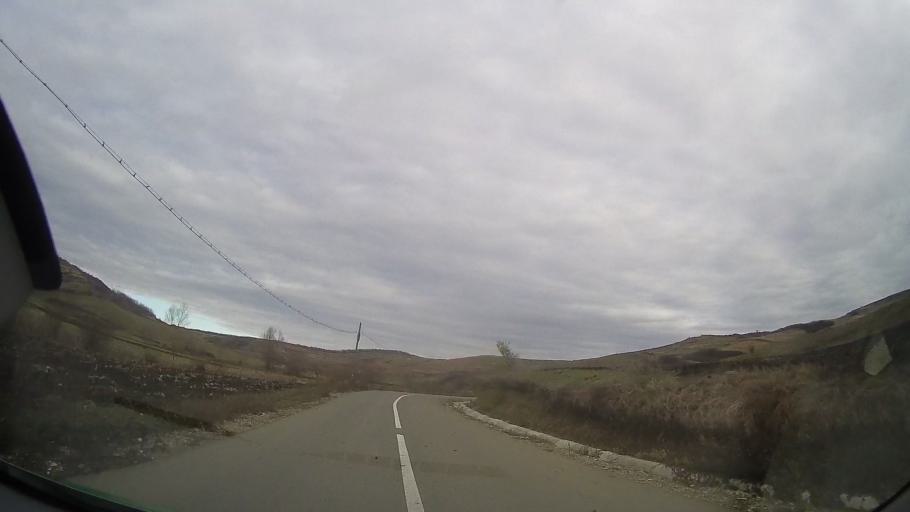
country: RO
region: Bistrita-Nasaud
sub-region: Comuna Silvasu de Campie
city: Silvasu de Campie
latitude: 46.8212
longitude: 24.2995
